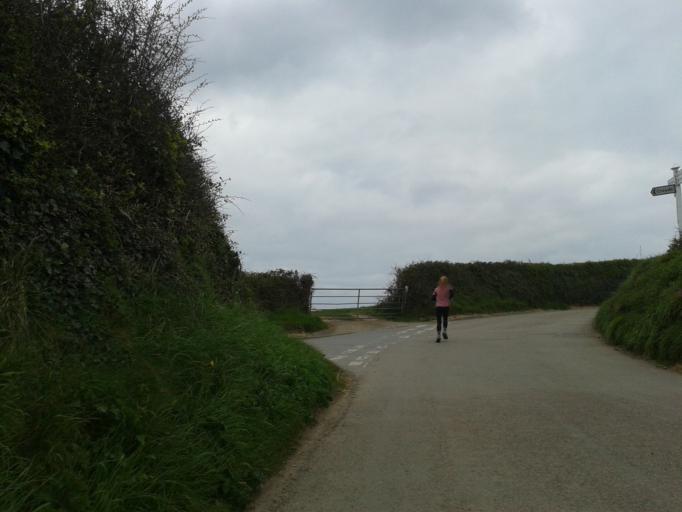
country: GB
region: England
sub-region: Devon
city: Braunton
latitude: 51.1400
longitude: -4.2211
